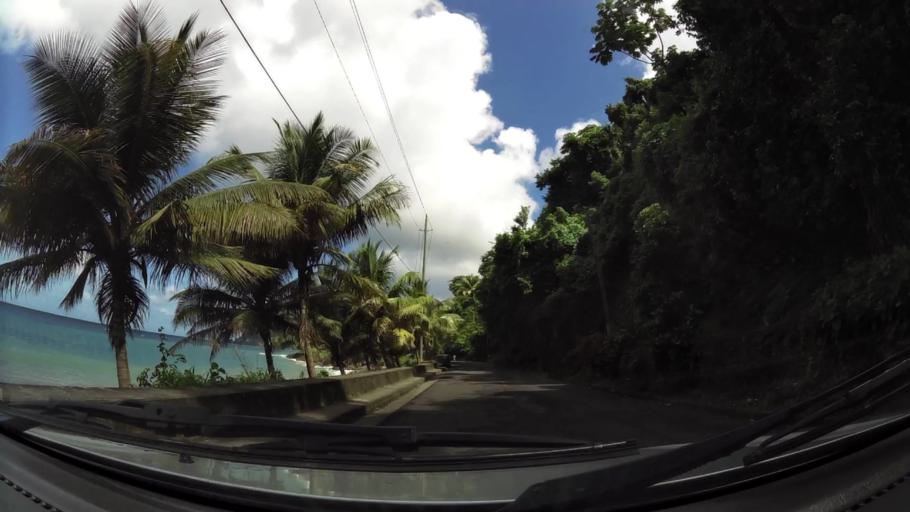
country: GD
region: Saint Mark
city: Victoria
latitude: 12.1939
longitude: -61.7096
